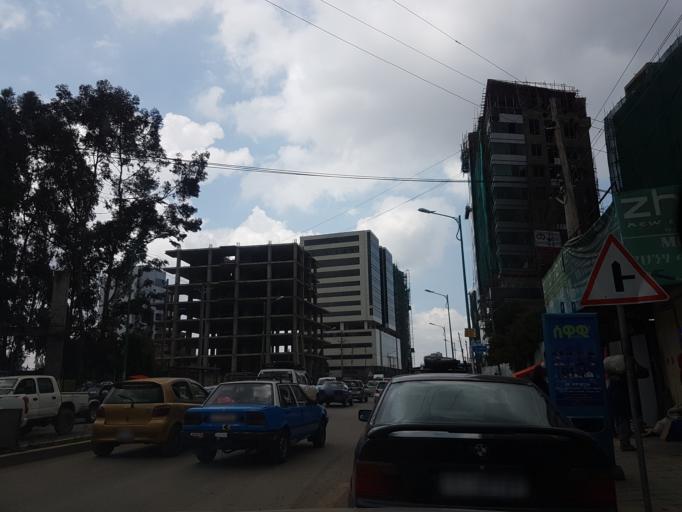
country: ET
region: Adis Abeba
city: Addis Ababa
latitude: 9.0027
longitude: 38.7676
